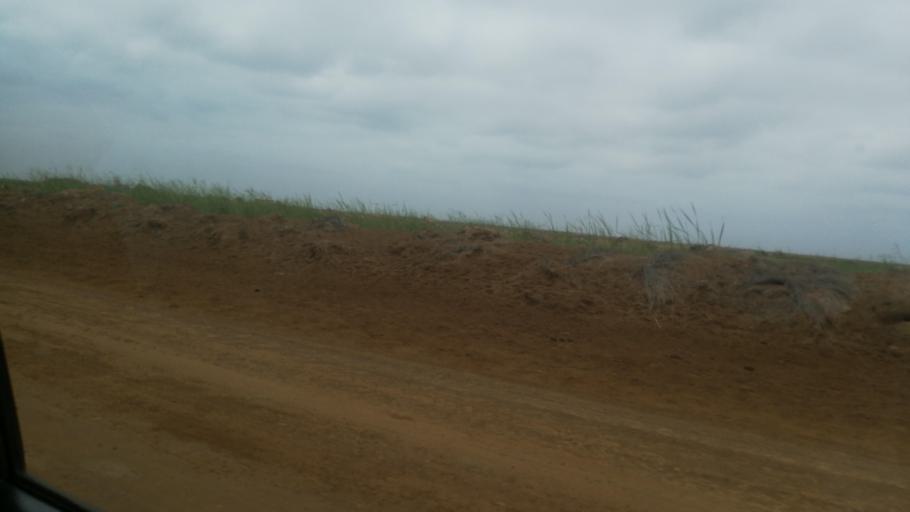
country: SN
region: Saint-Louis
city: Saint-Louis
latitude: 16.3164
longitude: -16.2331
